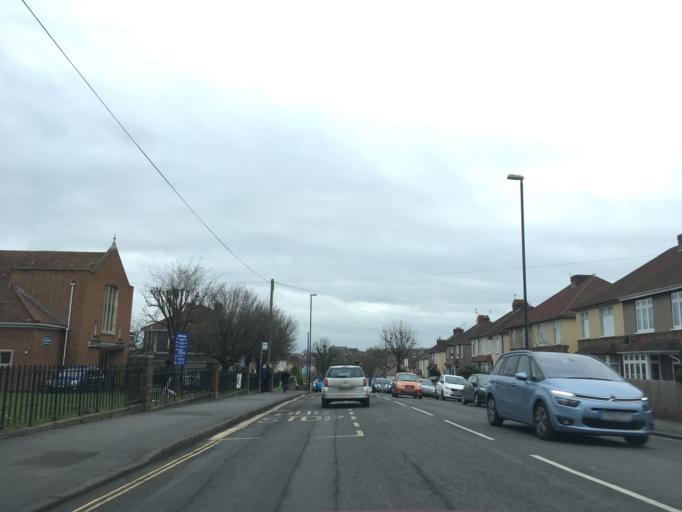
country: GB
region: England
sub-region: Bristol
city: Bristol
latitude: 51.4851
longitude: -2.5795
